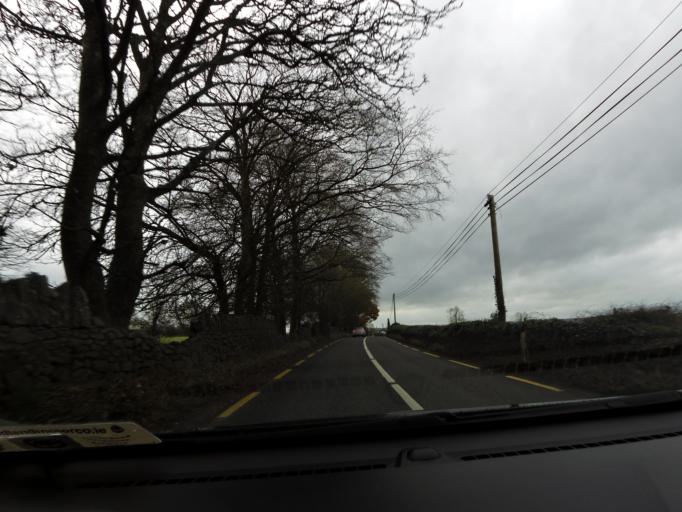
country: IE
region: Leinster
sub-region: Kilkenny
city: Ballyragget
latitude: 52.7455
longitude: -7.3224
